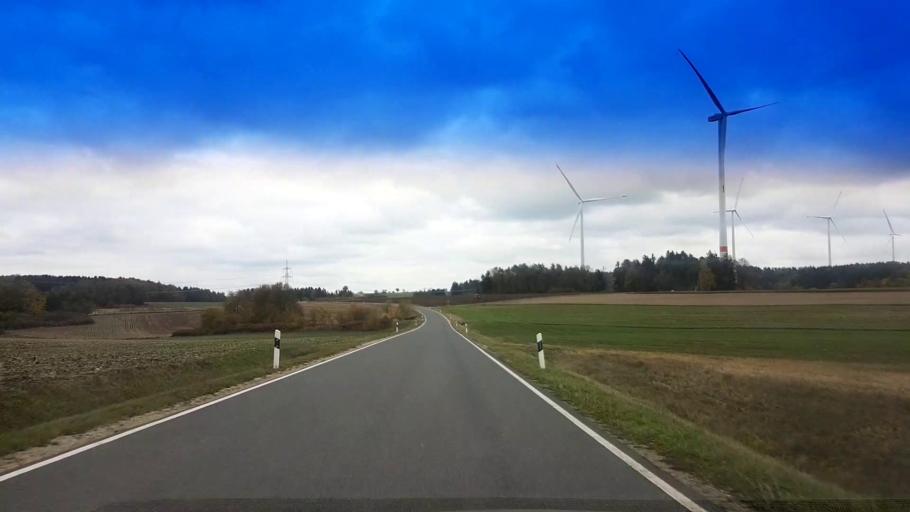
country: DE
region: Bavaria
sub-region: Upper Franconia
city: Poxdorf
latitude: 49.9476
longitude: 11.0943
